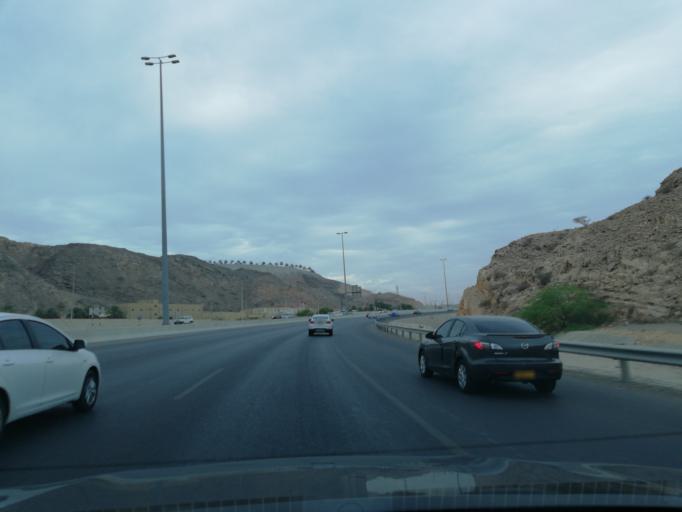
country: OM
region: Muhafazat Masqat
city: Bawshar
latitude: 23.6005
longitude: 58.4861
